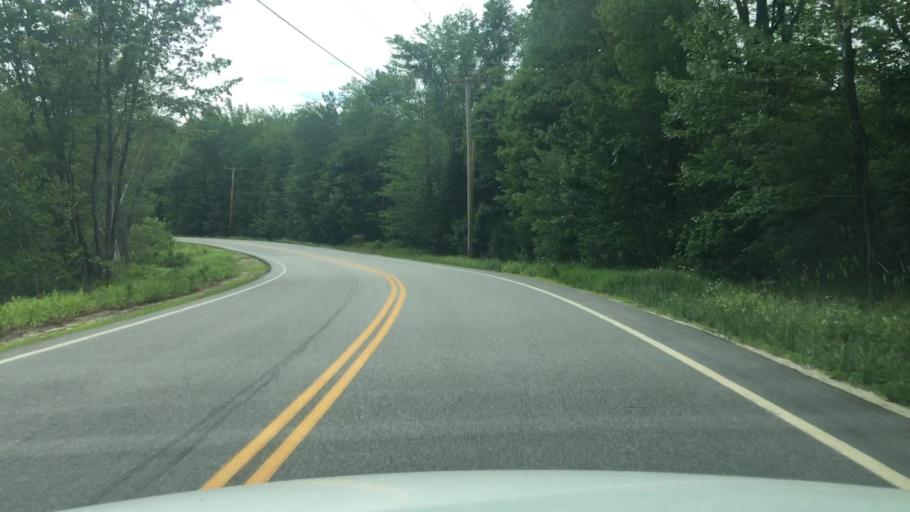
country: US
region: Maine
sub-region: Oxford County
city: West Paris
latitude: 44.3726
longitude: -70.4737
